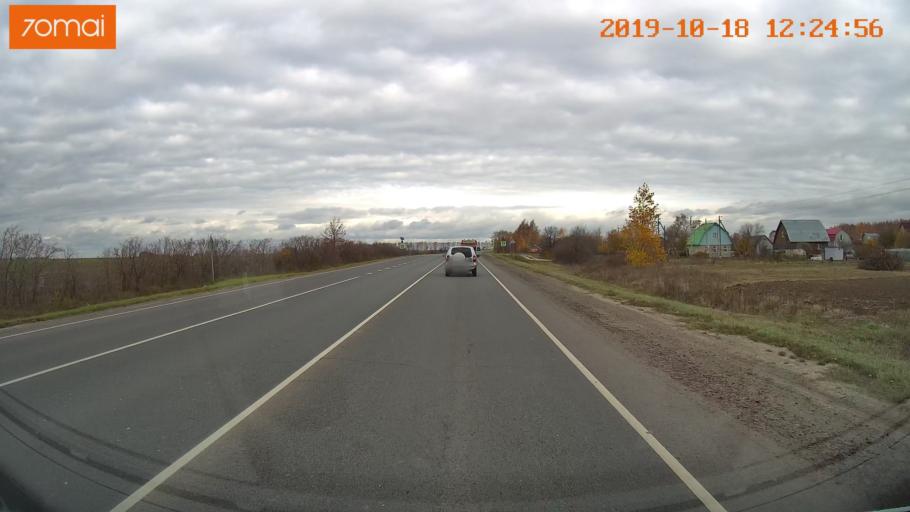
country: RU
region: Rjazan
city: Rybnoye
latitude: 54.5442
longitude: 39.5160
